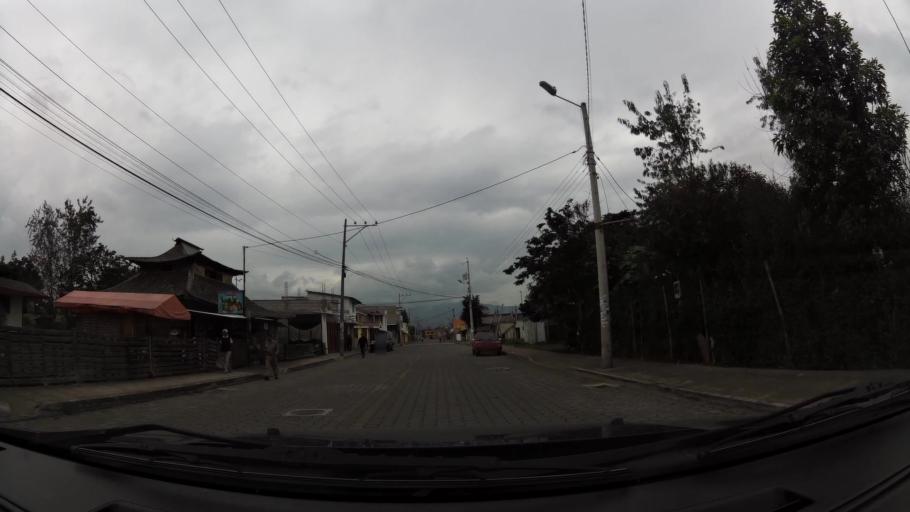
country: EC
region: Pichincha
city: Sangolqui
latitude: -0.3357
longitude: -78.4647
